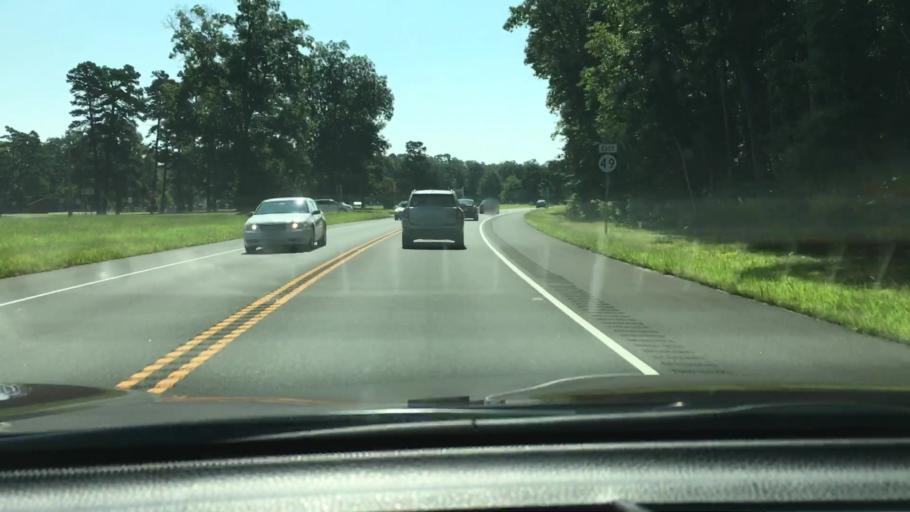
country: US
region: New Jersey
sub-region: Cape May County
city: Woodbine
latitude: 39.3120
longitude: -74.8239
